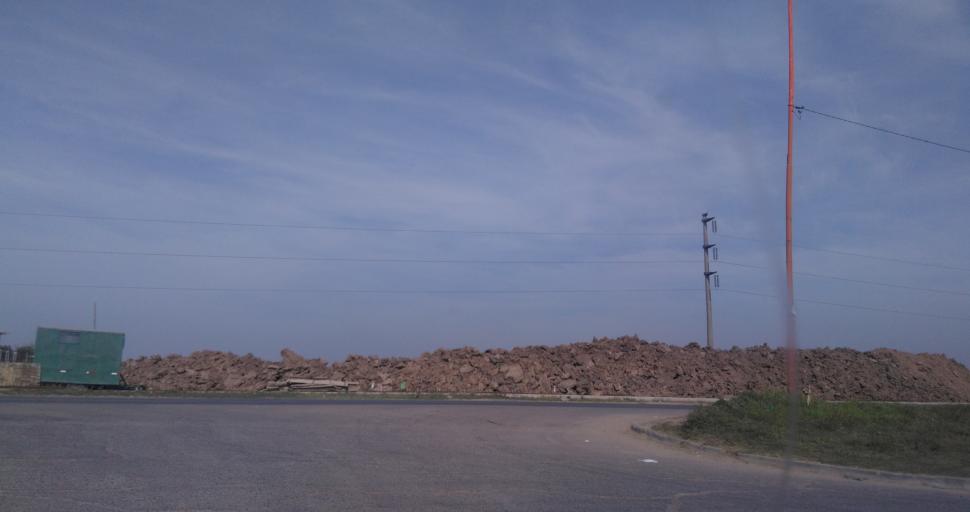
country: AR
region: Chaco
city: Fontana
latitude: -27.4480
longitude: -59.0260
